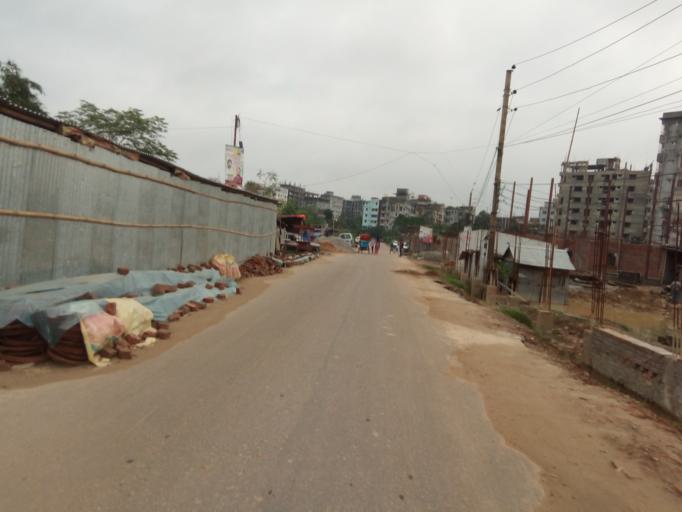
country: BD
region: Dhaka
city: Tungi
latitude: 23.8491
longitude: 90.4167
